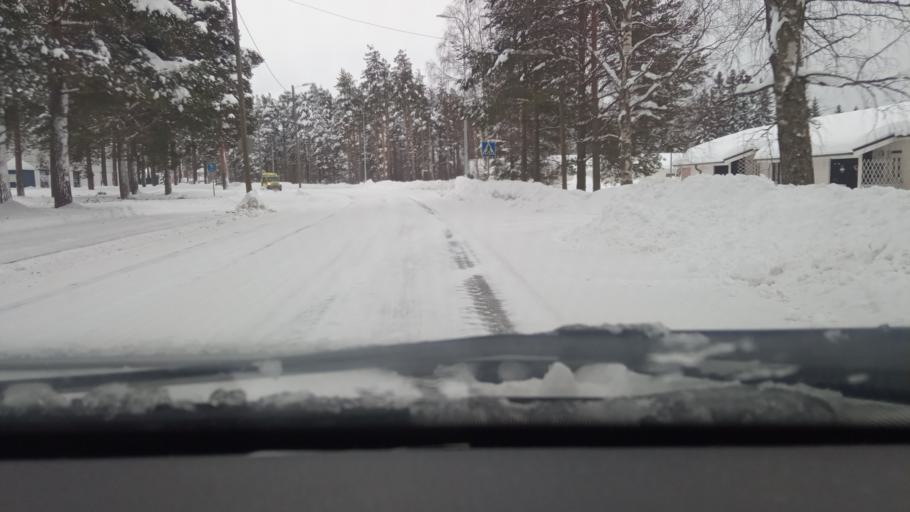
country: FI
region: Southern Ostrobothnia
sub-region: Jaerviseutu
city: Alajaervi
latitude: 62.9985
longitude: 23.8045
